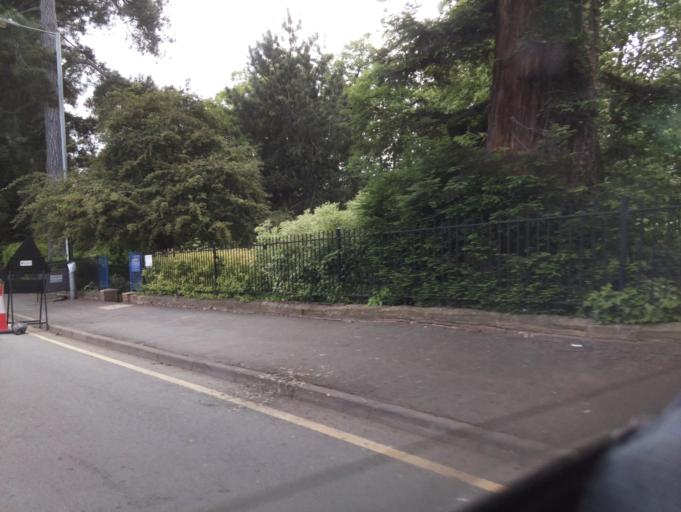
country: GB
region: England
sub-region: Worcestershire
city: Evesham
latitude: 52.0901
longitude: -1.9430
